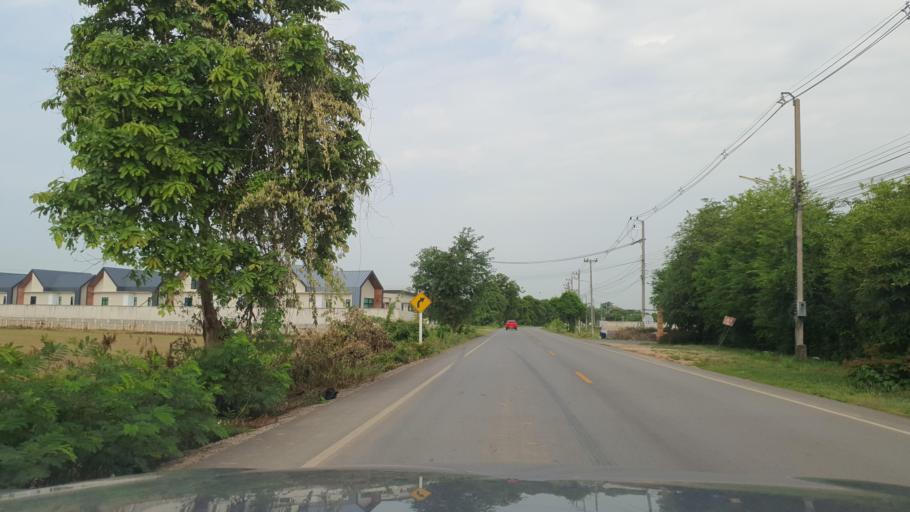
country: TH
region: Phitsanulok
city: Phitsanulok
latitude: 16.8142
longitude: 100.1888
